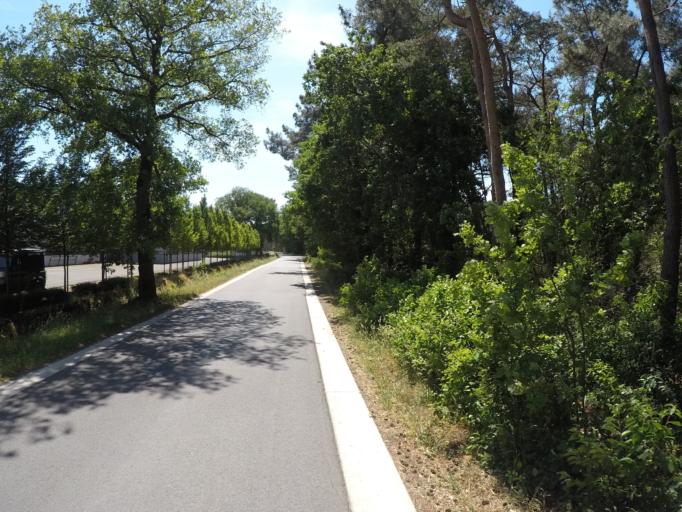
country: BE
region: Flanders
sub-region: Provincie Antwerpen
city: Wuustwezel
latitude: 51.3902
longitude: 4.5611
